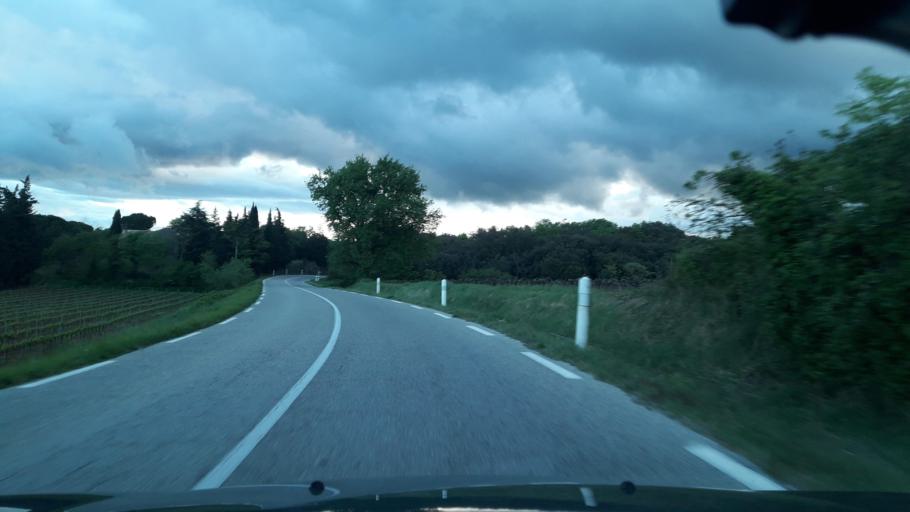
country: FR
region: Languedoc-Roussillon
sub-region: Departement du Gard
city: Sabran
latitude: 44.1432
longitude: 4.4820
